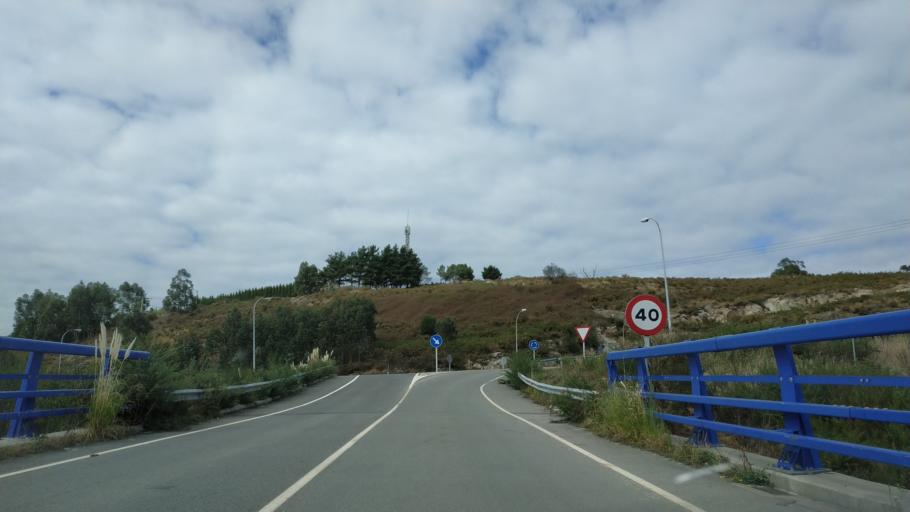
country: ES
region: Galicia
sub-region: Provincia da Coruna
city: Arteixo
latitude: 43.3295
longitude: -8.4592
